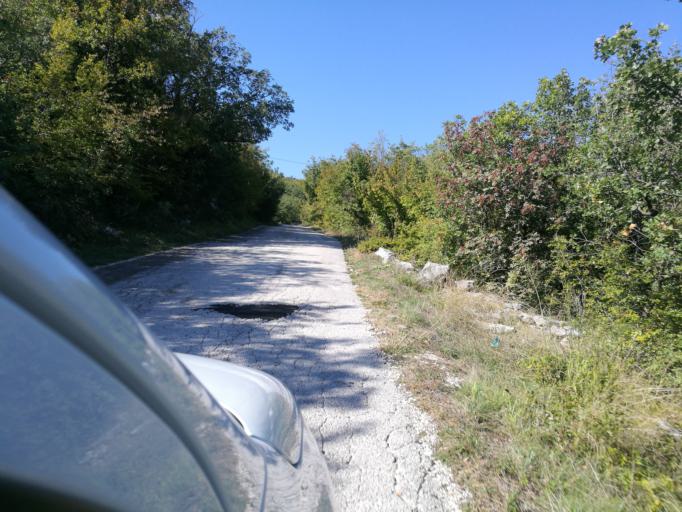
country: HR
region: Splitsko-Dalmatinska
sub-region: Grad Omis
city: Omis
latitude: 43.5148
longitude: 16.7294
